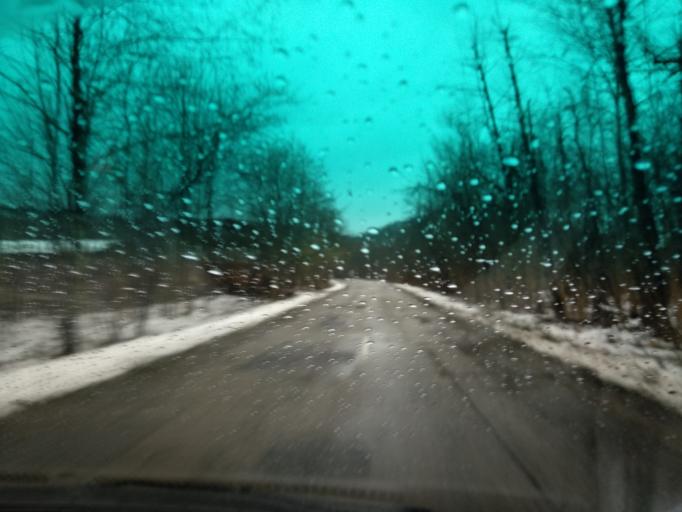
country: RU
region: Krasnodarskiy
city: Khadyzhensk
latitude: 44.2198
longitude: 39.3953
